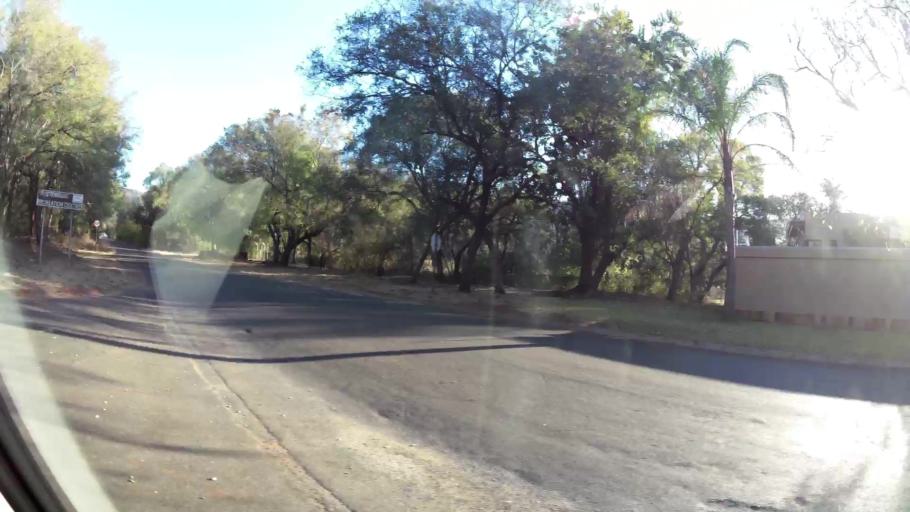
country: ZA
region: North-West
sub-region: Bojanala Platinum District Municipality
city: Rustenburg
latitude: -25.6912
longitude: 27.2053
